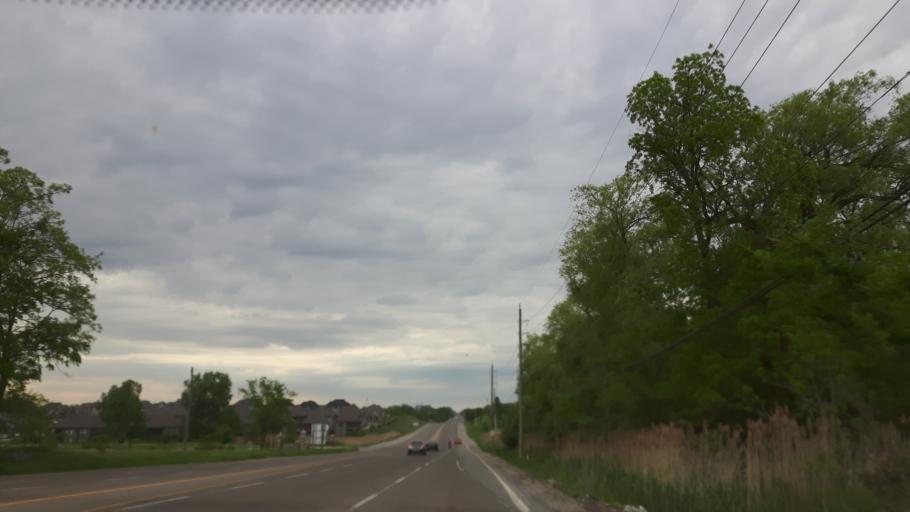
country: CA
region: Ontario
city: London
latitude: 43.0391
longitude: -81.2890
